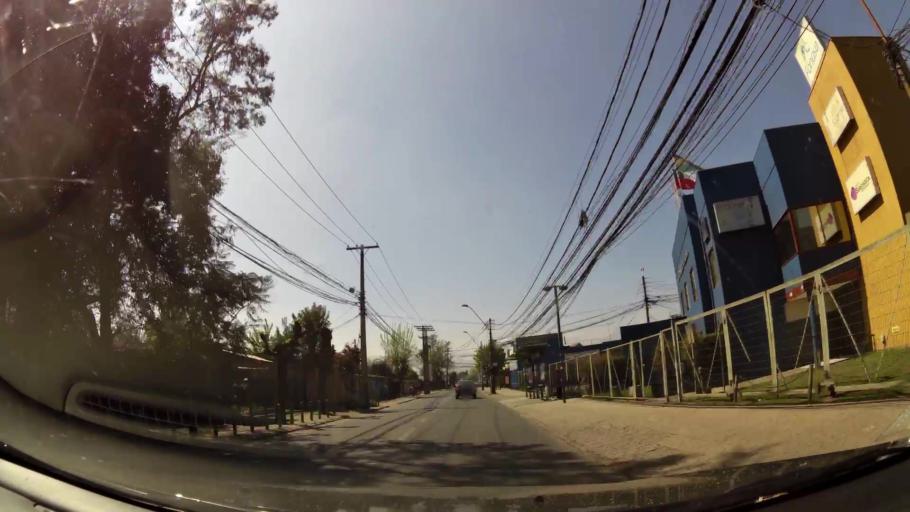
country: CL
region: Santiago Metropolitan
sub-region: Provincia de Santiago
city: Lo Prado
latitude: -33.3686
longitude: -70.7281
